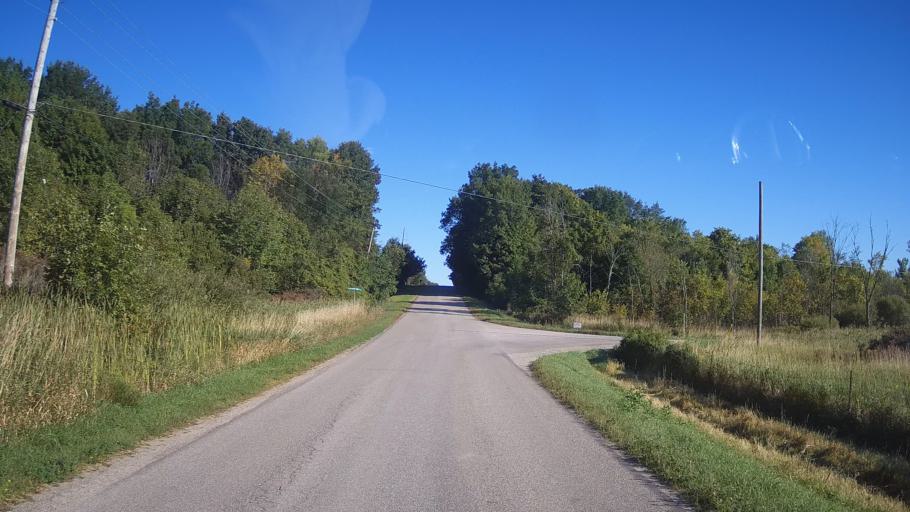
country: US
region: New York
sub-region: Jefferson County
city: Alexandria Bay
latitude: 44.4426
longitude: -75.9834
